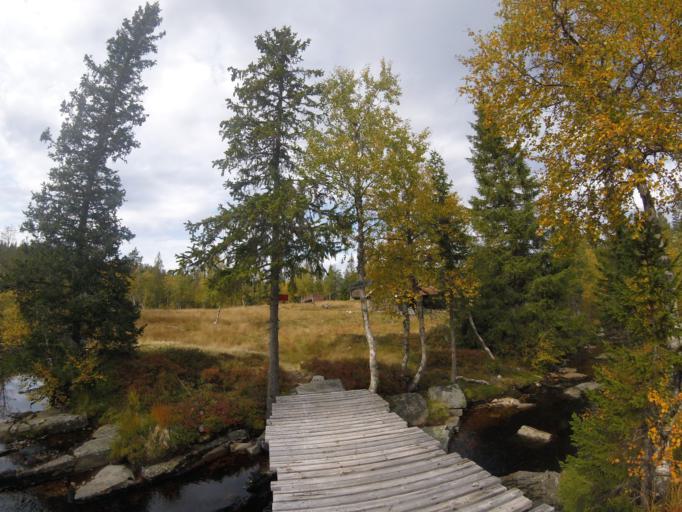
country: NO
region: Buskerud
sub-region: Rollag
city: Rollag
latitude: 59.8167
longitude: 9.3414
